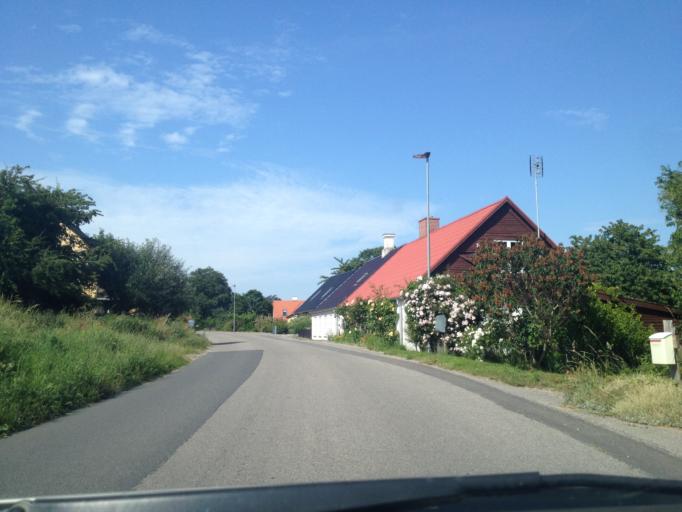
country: DK
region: Central Jutland
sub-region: Samso Kommune
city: Tranebjerg
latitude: 55.8218
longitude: 10.5575
